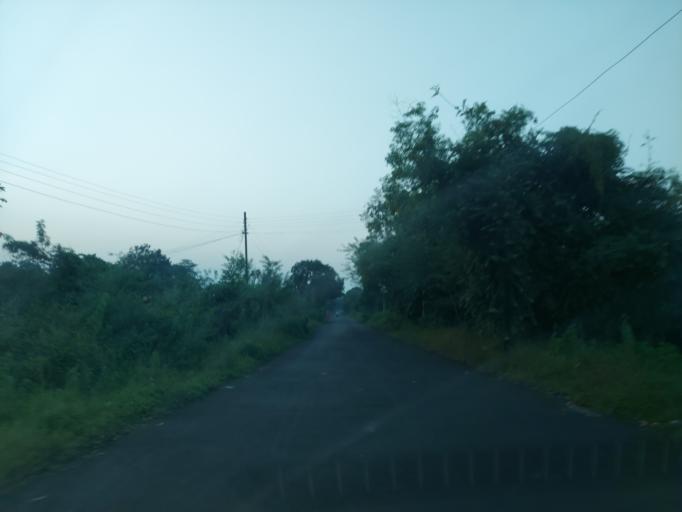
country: IN
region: Maharashtra
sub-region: Sindhudurg
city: Kudal
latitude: 16.1039
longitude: 73.7077
